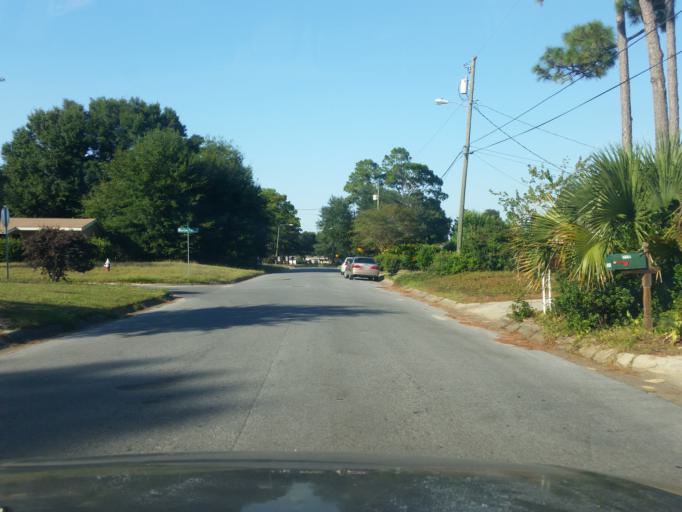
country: US
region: Florida
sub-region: Escambia County
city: Ferry Pass
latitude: 30.4918
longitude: -87.1746
